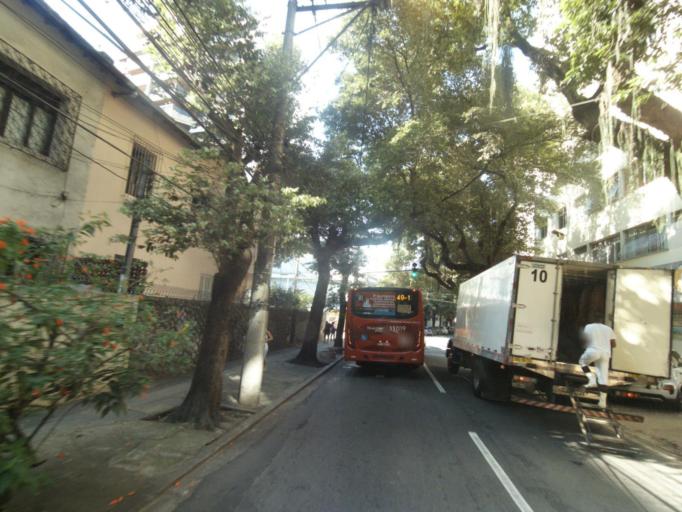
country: BR
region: Rio de Janeiro
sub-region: Niteroi
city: Niteroi
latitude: -22.9011
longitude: -43.1254
